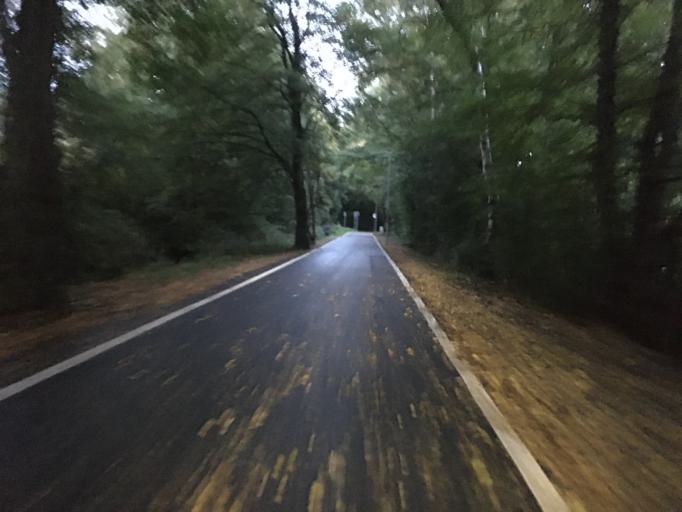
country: DE
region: North Rhine-Westphalia
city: Hattingen
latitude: 51.4421
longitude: 7.1823
